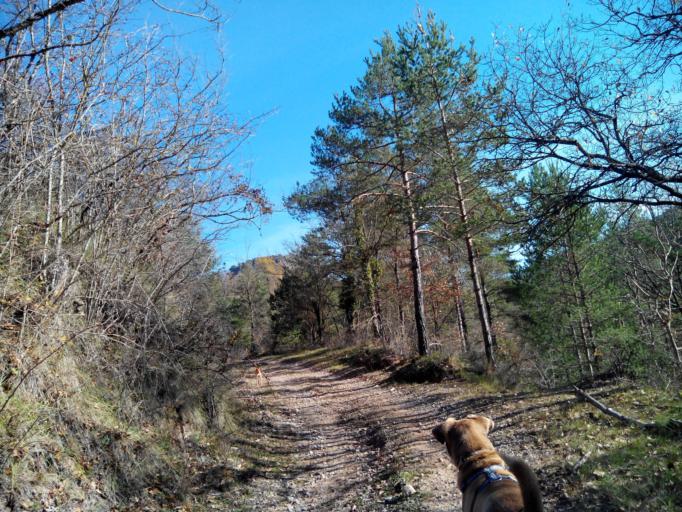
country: ES
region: Catalonia
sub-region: Provincia de Barcelona
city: Vilada
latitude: 42.1038
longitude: 1.9467
